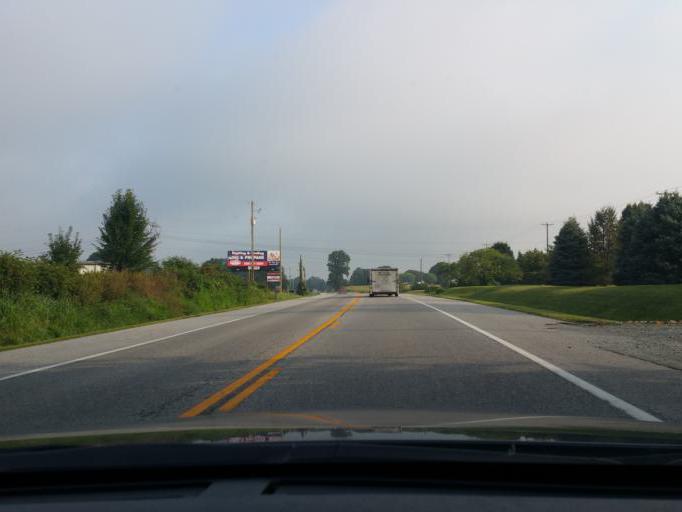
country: US
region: Maryland
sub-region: Cecil County
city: Rising Sun
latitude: 39.6772
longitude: -76.0738
